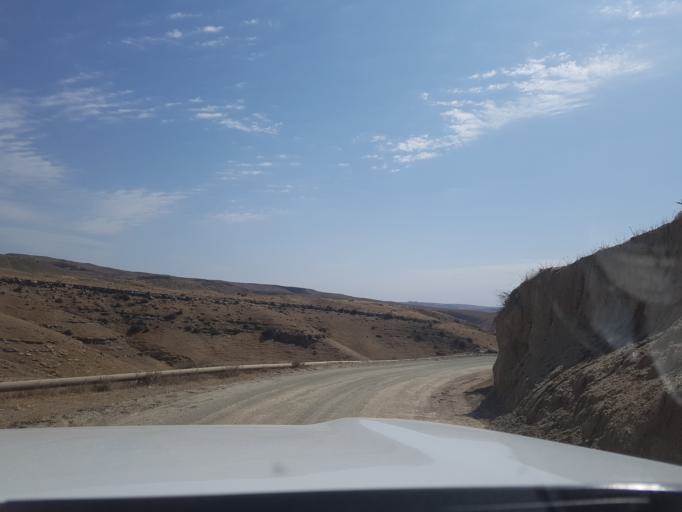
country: TM
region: Ahal
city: Baharly
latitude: 38.2500
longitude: 56.8917
